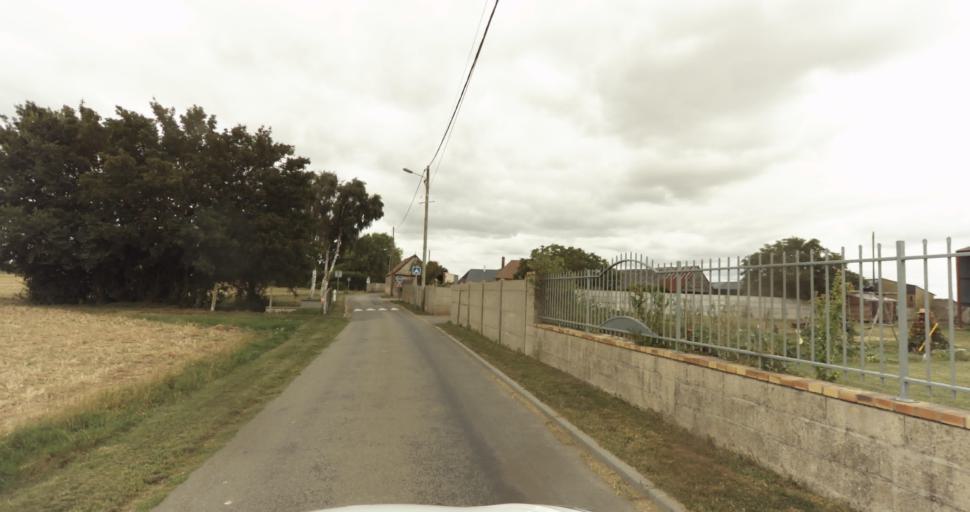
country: FR
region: Haute-Normandie
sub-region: Departement de l'Eure
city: La Madeleine-de-Nonancourt
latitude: 48.8209
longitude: 1.2048
